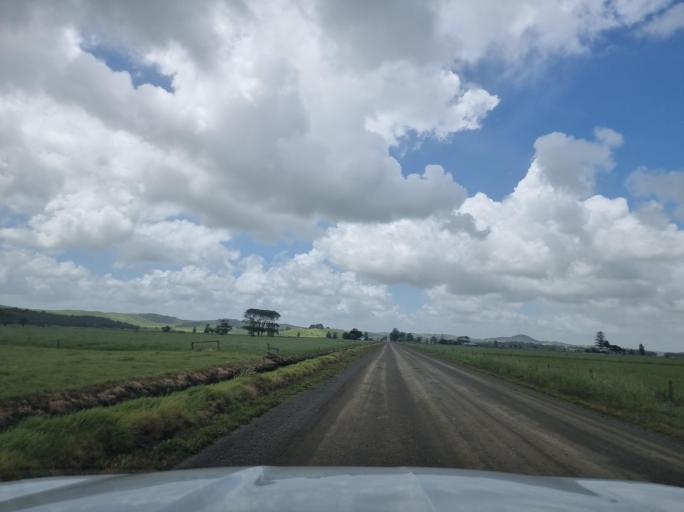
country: NZ
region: Northland
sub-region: Kaipara District
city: Dargaville
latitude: -36.0866
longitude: 174.0302
